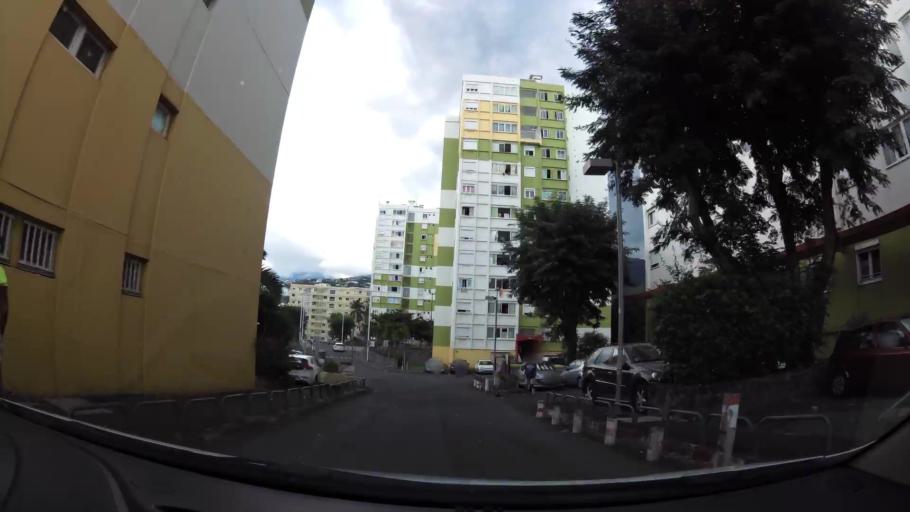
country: RE
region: Reunion
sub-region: Reunion
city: Saint-Denis
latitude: -20.8901
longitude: 55.4576
